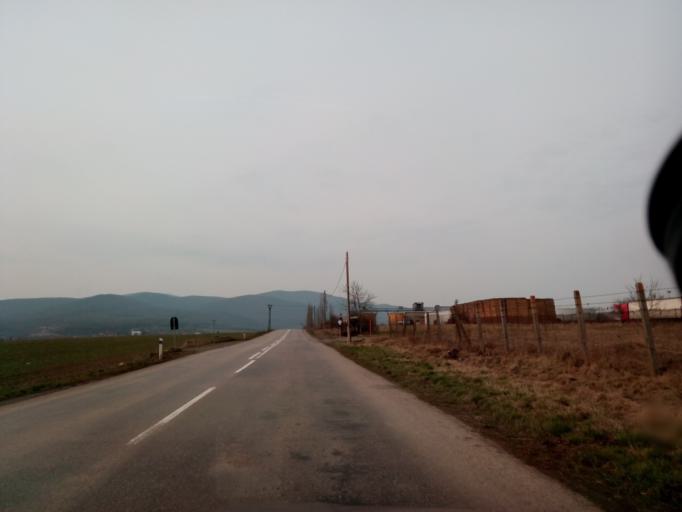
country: SK
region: Kosicky
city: Secovce
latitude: 48.6362
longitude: 21.5818
